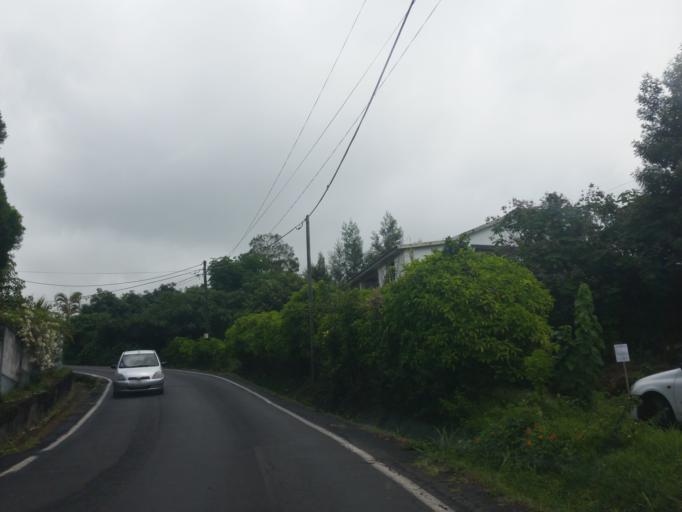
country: RE
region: Reunion
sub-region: Reunion
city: Le Tampon
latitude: -21.2415
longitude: 55.5110
